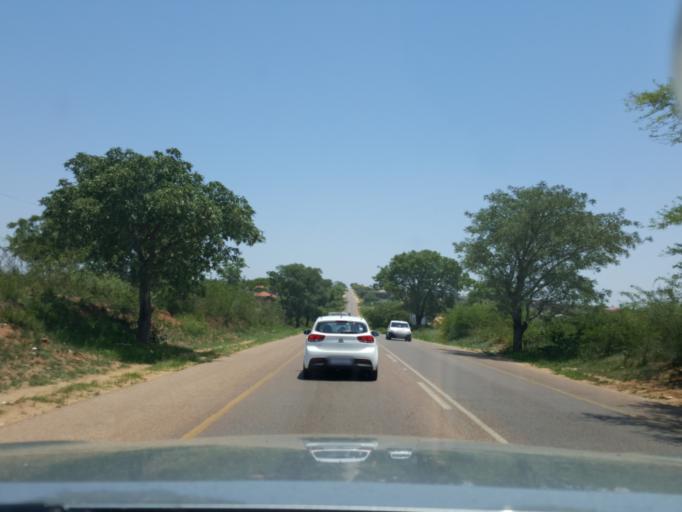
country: ZA
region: Limpopo
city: Thulamahashi
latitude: -24.6354
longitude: 31.0417
